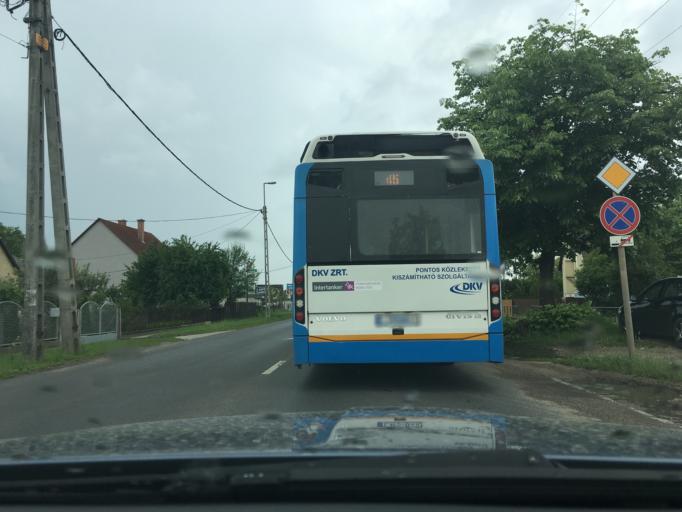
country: HU
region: Hajdu-Bihar
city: Debrecen
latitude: 47.5304
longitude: 21.6697
